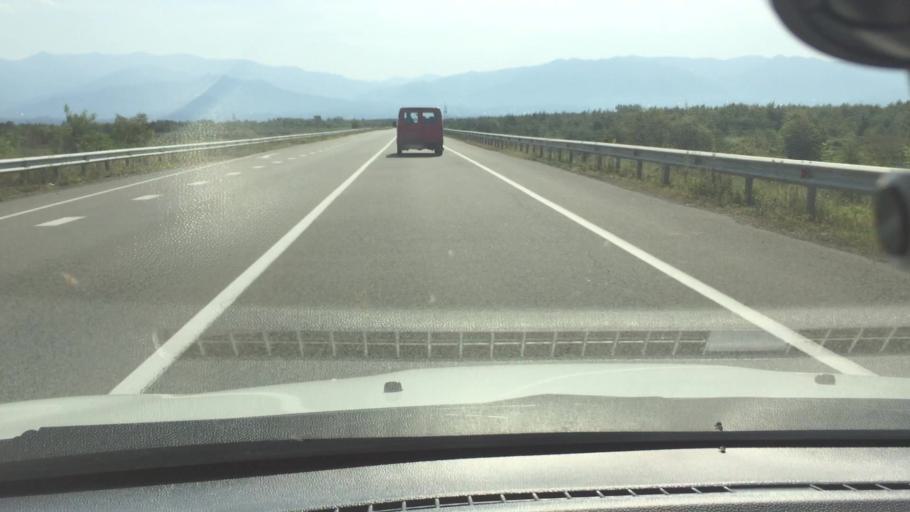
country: GE
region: Ajaria
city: Ochkhamuri
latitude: 41.8987
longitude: 41.7971
